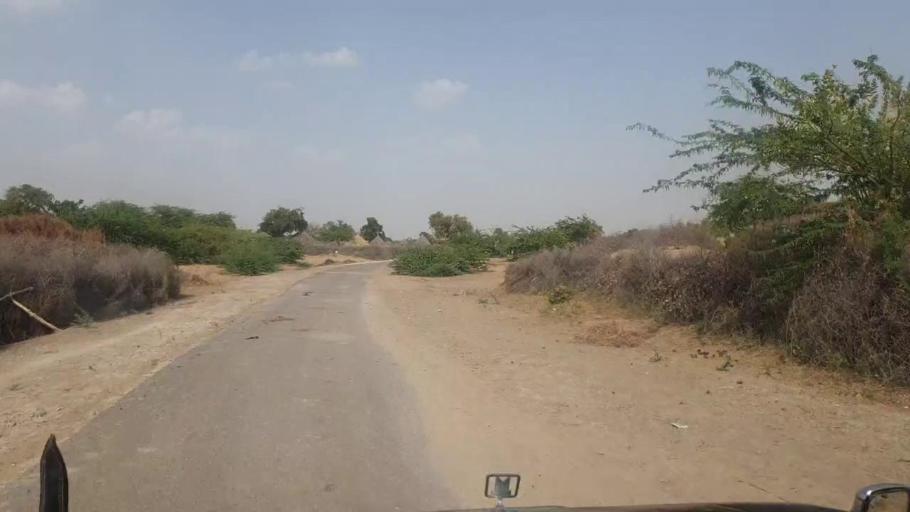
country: PK
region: Sindh
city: Islamkot
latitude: 25.2336
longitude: 70.2856
